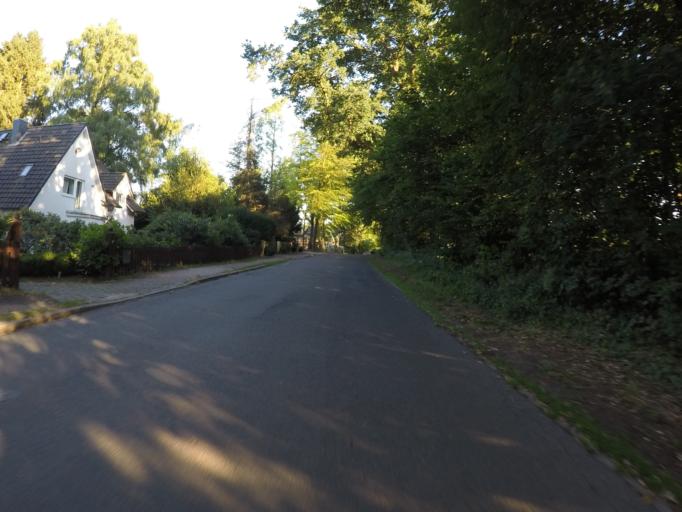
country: DE
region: Hamburg
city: Wohldorf-Ohlstedt
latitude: 53.6895
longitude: 10.1143
